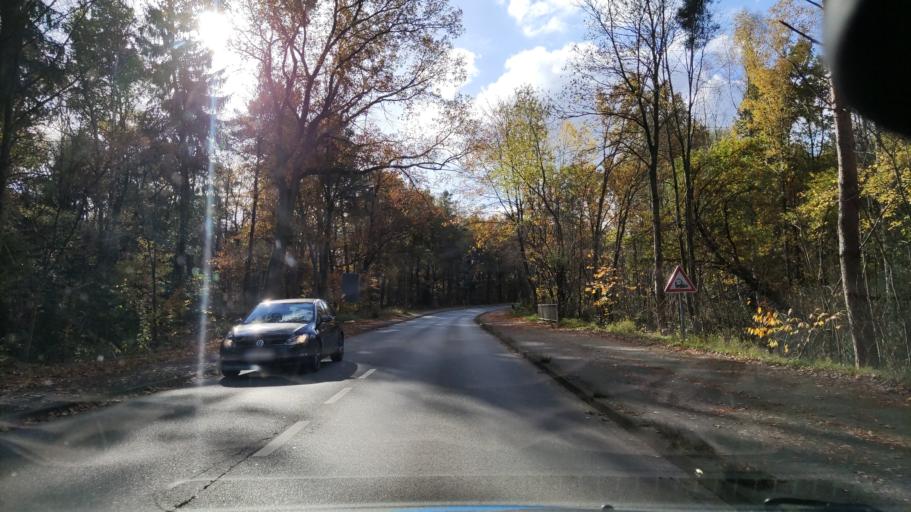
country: DE
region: Lower Saxony
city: Munster
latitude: 52.9929
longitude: 10.1103
